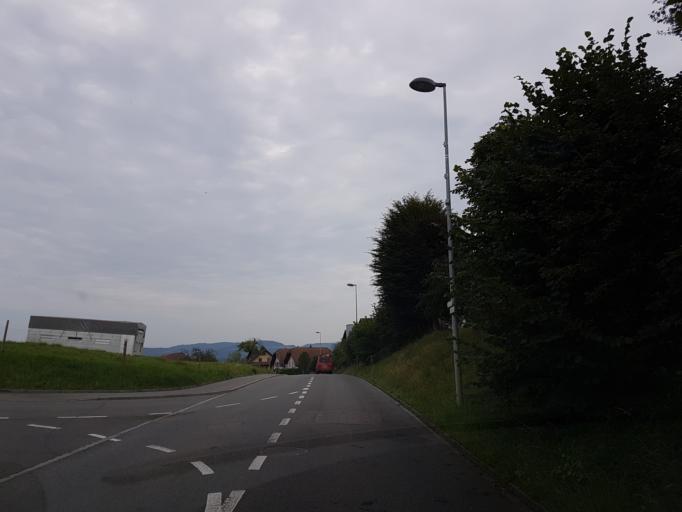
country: CH
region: Aargau
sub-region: Bezirk Muri
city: Merenschwand
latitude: 47.2479
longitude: 8.3672
